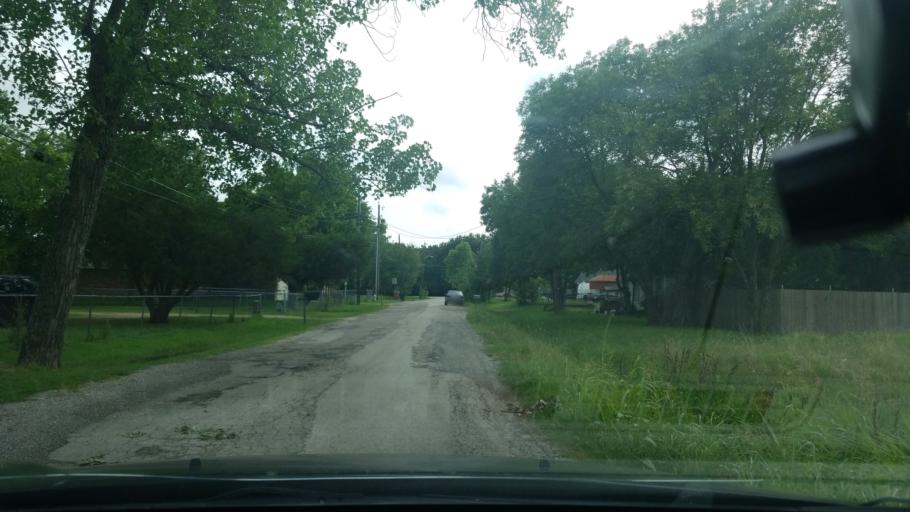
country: US
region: Texas
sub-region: Dallas County
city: Balch Springs
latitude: 32.7528
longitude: -96.6338
